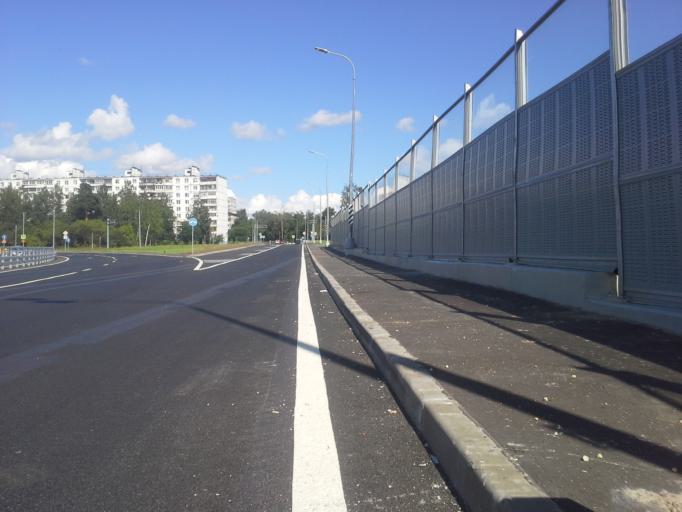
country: RU
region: Moskovskaya
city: Kokoshkino
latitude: 55.5959
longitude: 37.1561
